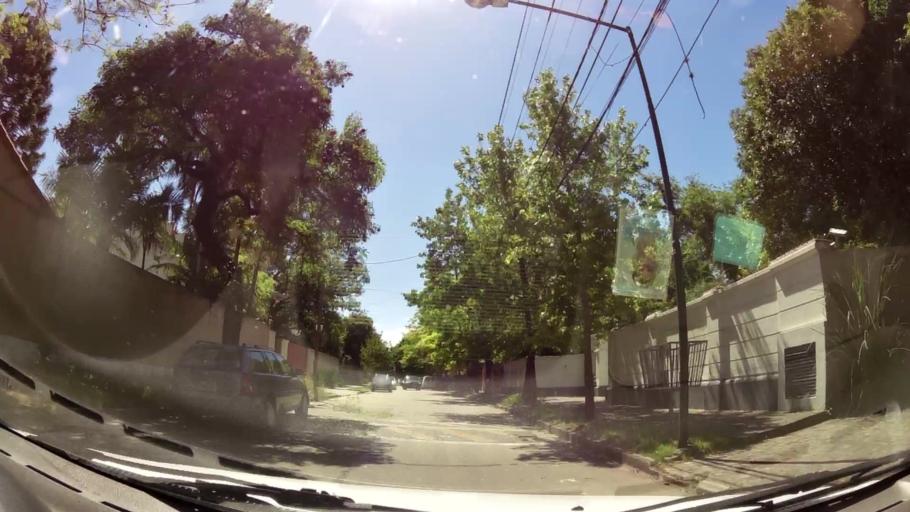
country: AR
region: Buenos Aires
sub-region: Partido de San Isidro
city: San Isidro
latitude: -34.4744
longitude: -58.4959
